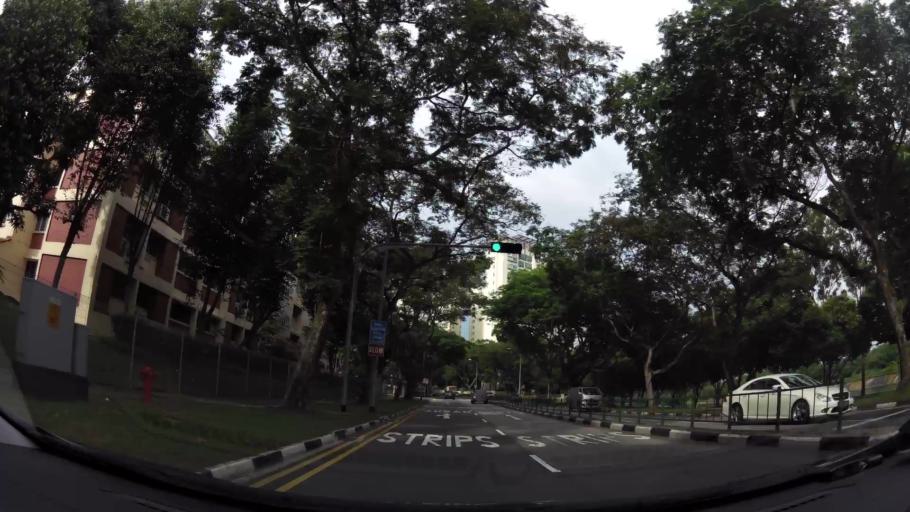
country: SG
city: Singapore
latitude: 1.3707
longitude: 103.9006
